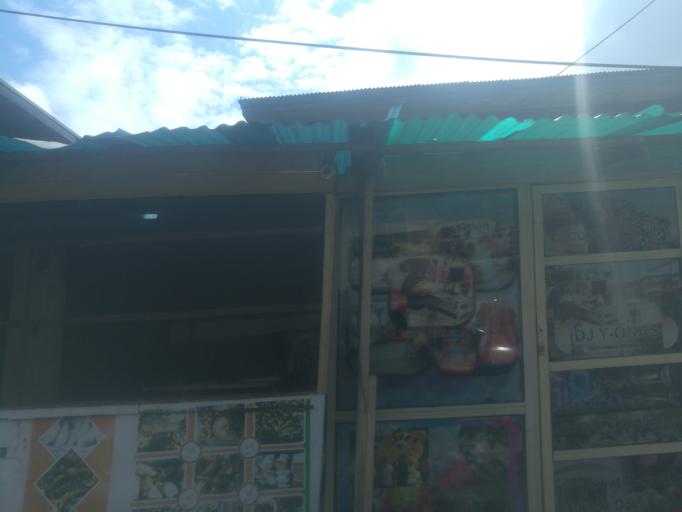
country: NG
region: Lagos
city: Somolu
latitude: 6.5482
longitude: 3.3744
